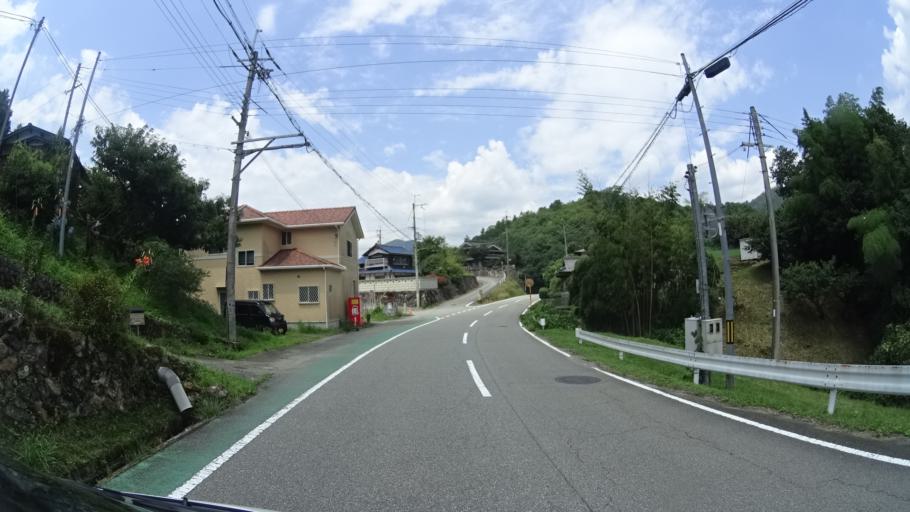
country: JP
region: Hyogo
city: Sasayama
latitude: 35.1673
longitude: 135.2613
